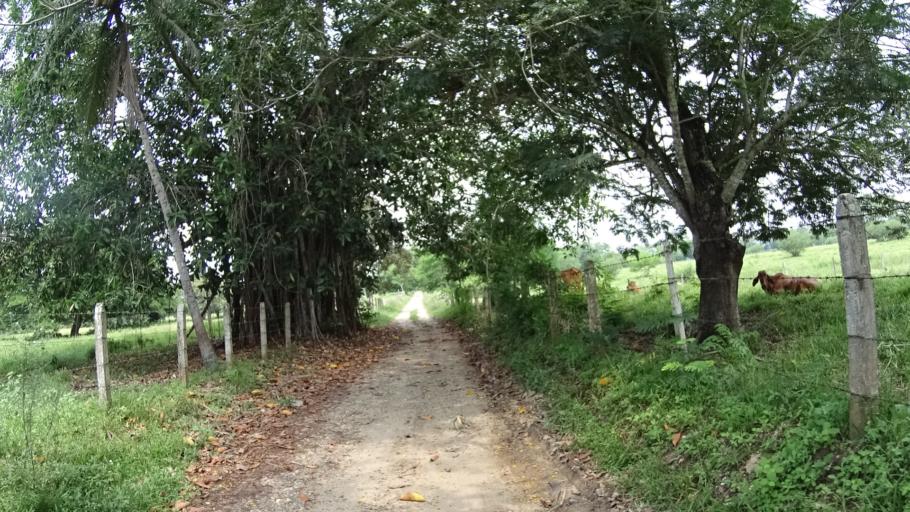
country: CO
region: Cundinamarca
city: Puerto Salgar
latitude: 5.5427
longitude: -74.6628
